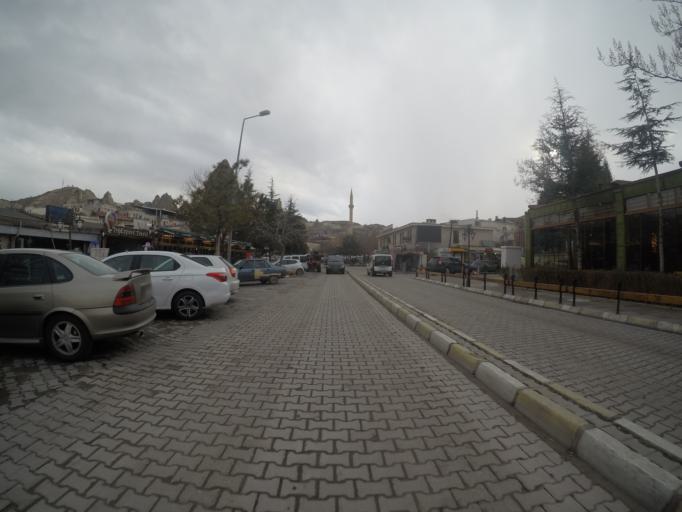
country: TR
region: Nevsehir
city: Goereme
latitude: 38.6432
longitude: 34.8292
